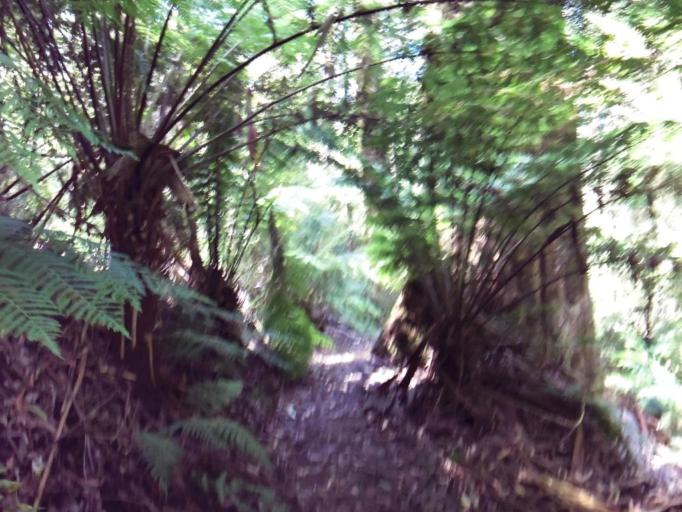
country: AU
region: Victoria
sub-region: Yarra Ranges
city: Mount Dandenong
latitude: -37.8346
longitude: 145.3671
